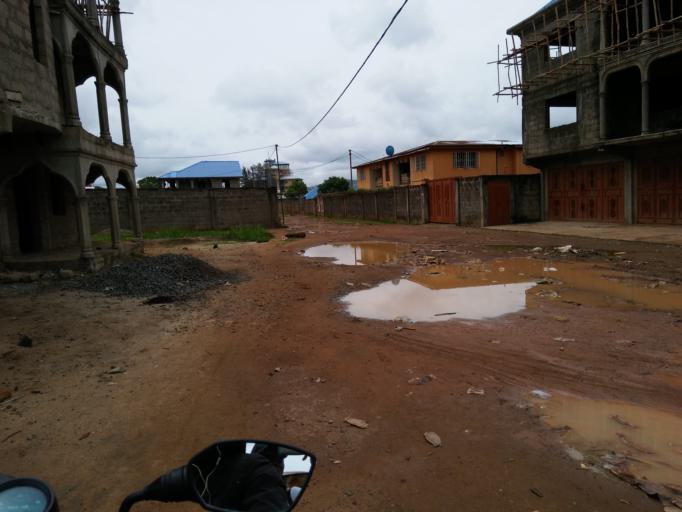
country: SL
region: Western Area
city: Hastings
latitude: 8.3969
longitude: -13.1537
